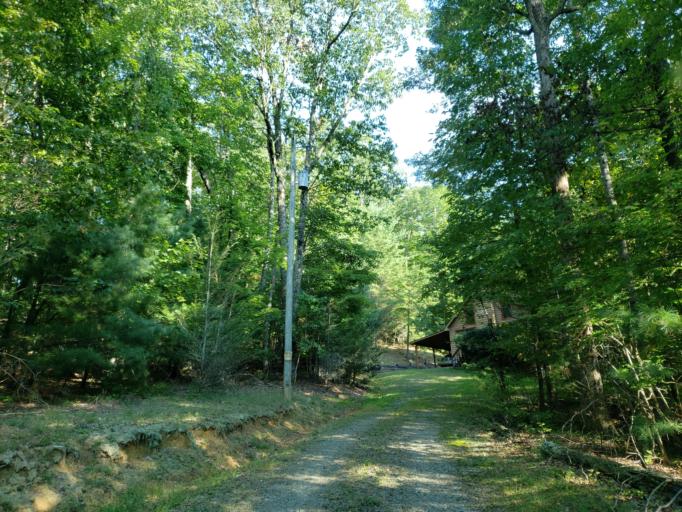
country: US
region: Georgia
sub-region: Fannin County
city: Blue Ridge
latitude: 34.6732
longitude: -84.2634
